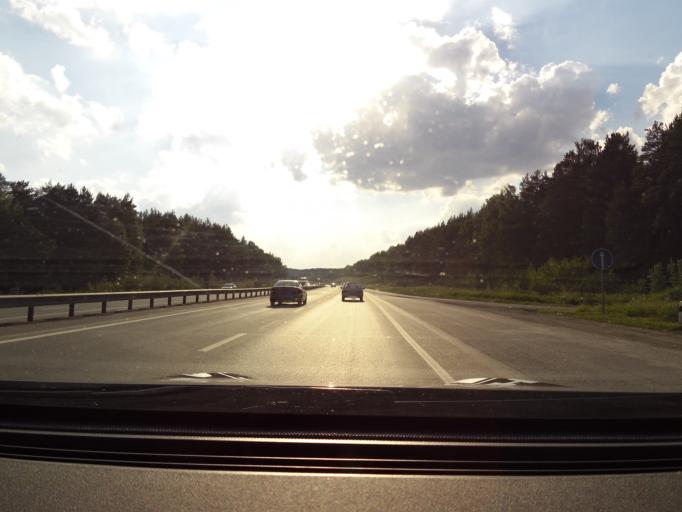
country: RU
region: Sverdlovsk
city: Severka
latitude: 56.8444
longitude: 60.2337
